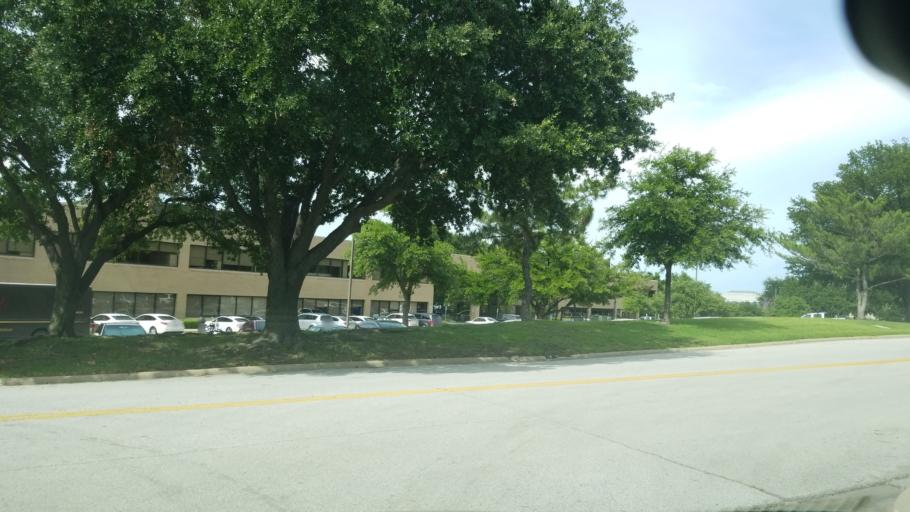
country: US
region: Texas
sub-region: Dallas County
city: Irving
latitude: 32.8817
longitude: -96.9768
